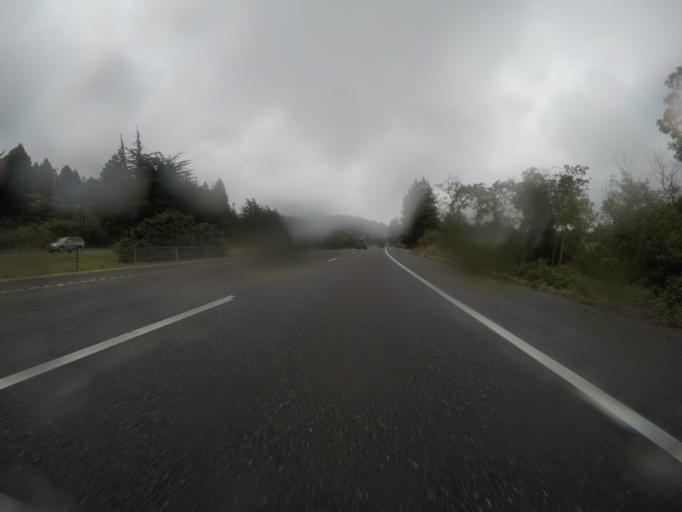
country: US
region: California
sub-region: Humboldt County
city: Arcata
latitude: 40.8907
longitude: -124.0802
